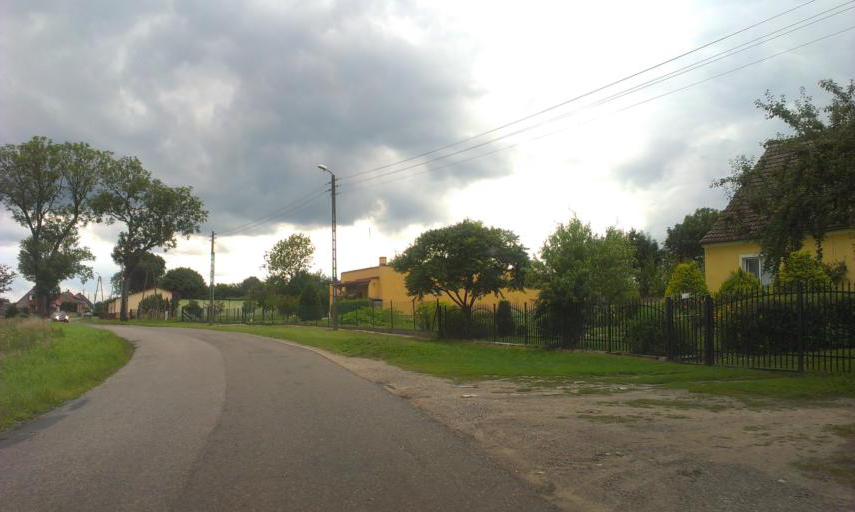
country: PL
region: West Pomeranian Voivodeship
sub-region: Powiat bialogardzki
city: Tychowo
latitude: 53.8972
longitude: 16.2071
